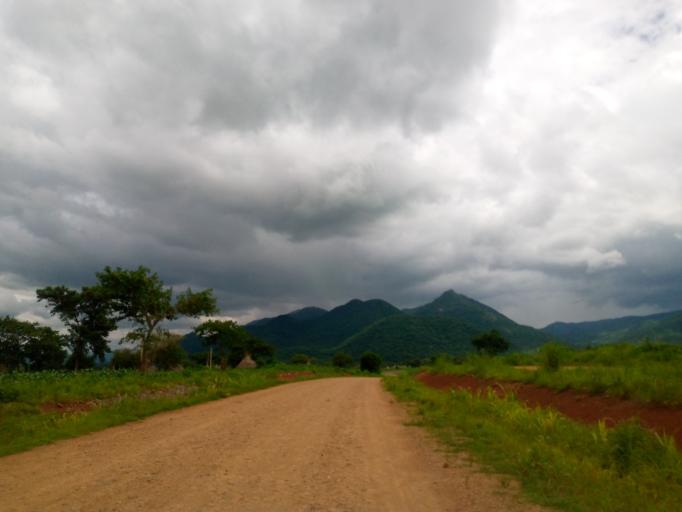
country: ET
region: Oromiya
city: Mendi
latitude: 10.1841
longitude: 35.0931
